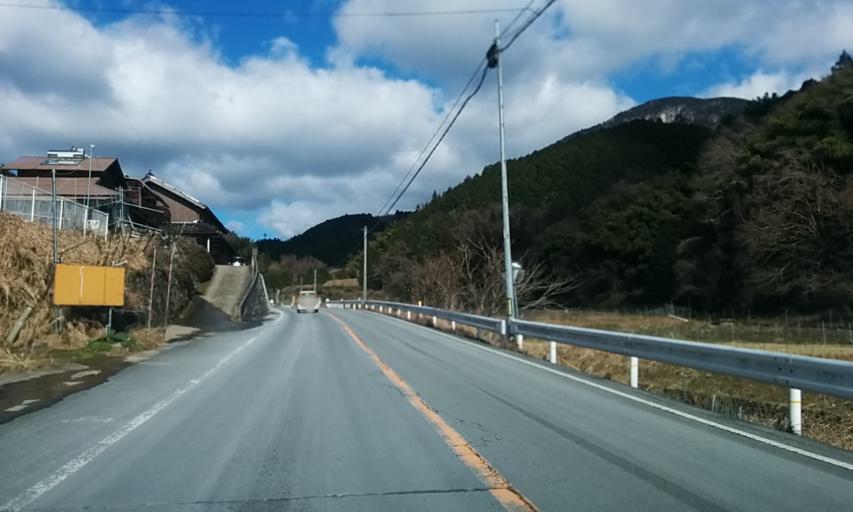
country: JP
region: Kyoto
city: Fukuchiyama
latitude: 35.3762
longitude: 135.0452
